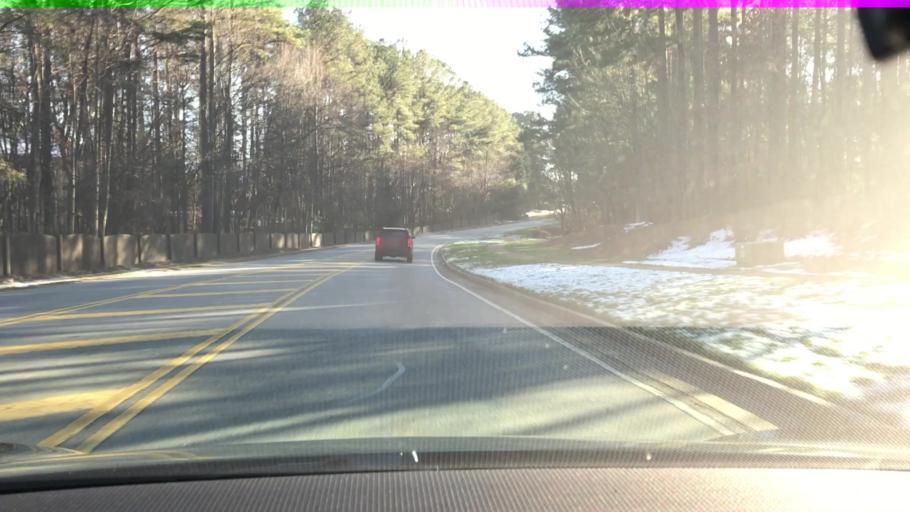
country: US
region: Georgia
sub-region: Gwinnett County
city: Suwanee
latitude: 34.0687
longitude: -84.0899
